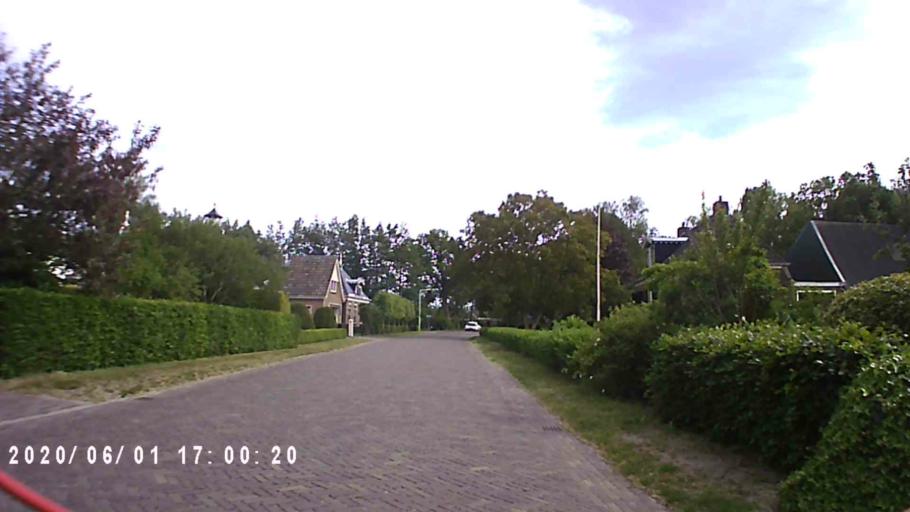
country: NL
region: Friesland
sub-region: Gemeente Tytsjerksteradiel
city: Hurdegaryp
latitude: 53.1833
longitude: 5.9294
